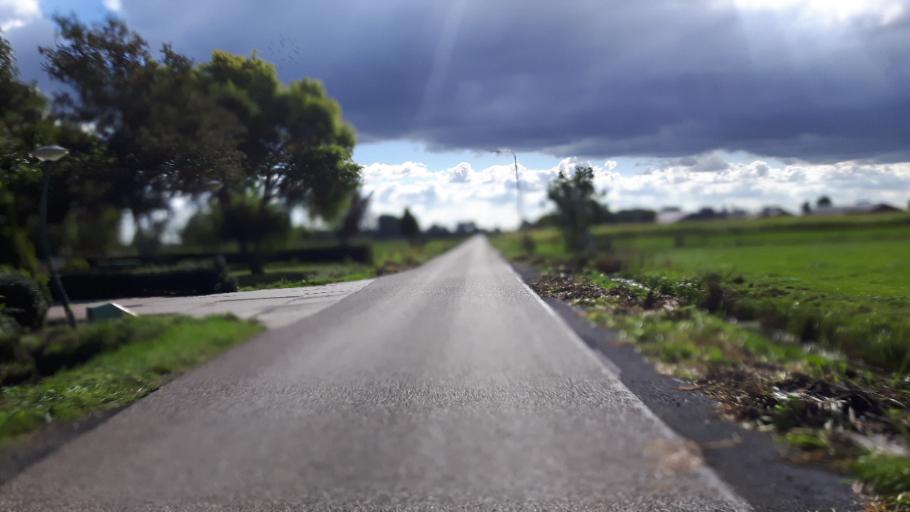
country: NL
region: South Holland
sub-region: Gemeente Leerdam
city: Leerdam
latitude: 51.9077
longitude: 5.1591
